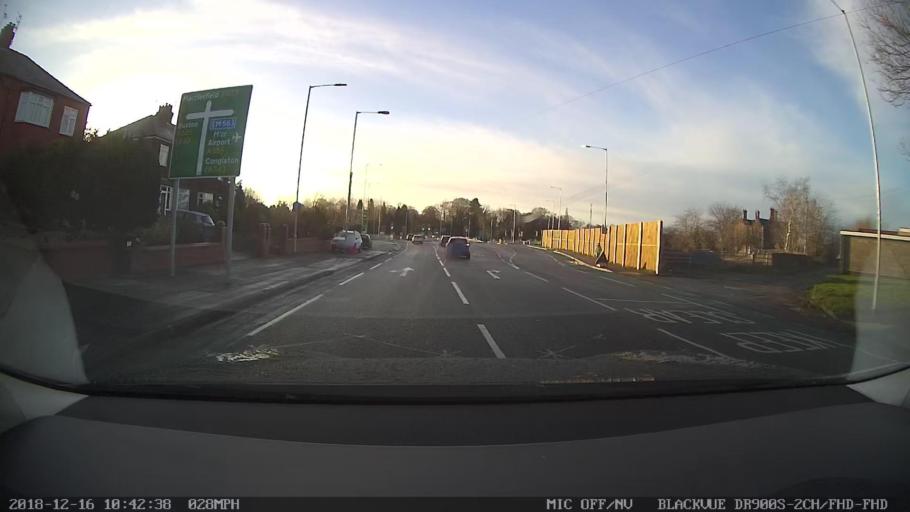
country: GB
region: England
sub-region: Cheshire East
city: Poynton
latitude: 53.3664
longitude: -2.1137
